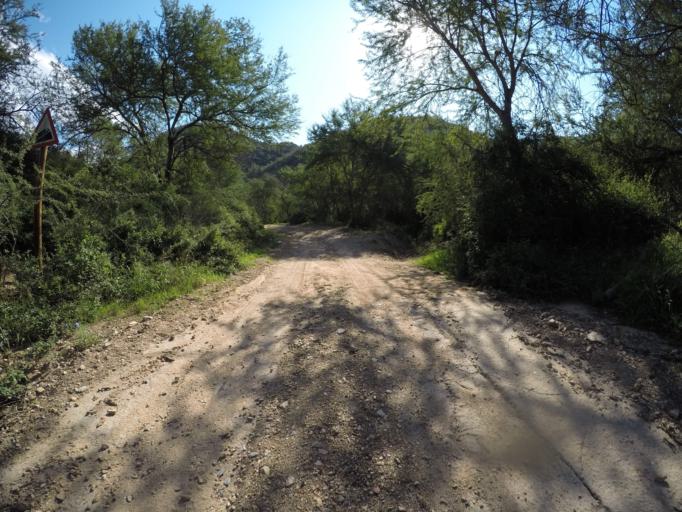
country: ZA
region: Eastern Cape
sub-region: Cacadu District Municipality
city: Kareedouw
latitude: -33.6548
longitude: 24.3650
